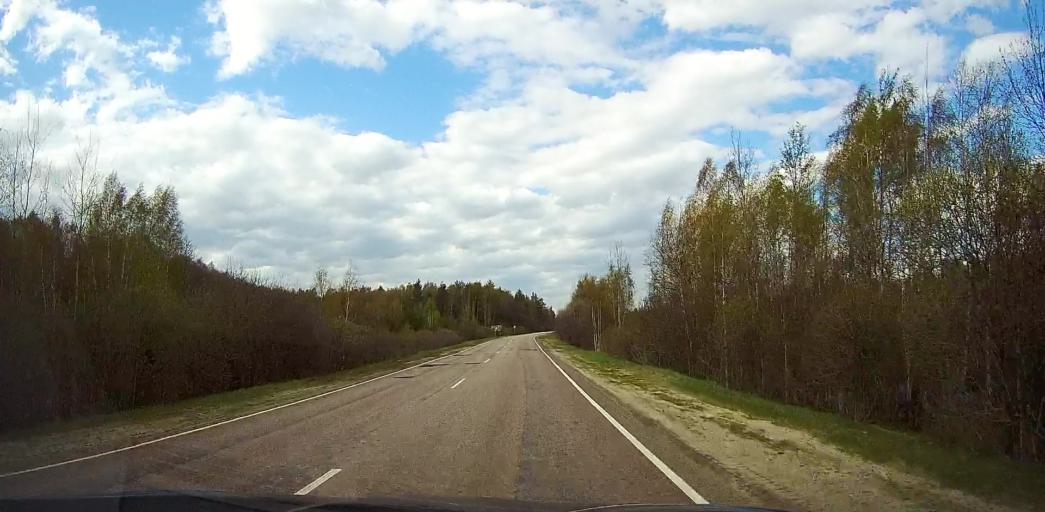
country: RU
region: Moskovskaya
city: Rakhmanovo
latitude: 55.6792
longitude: 38.6437
